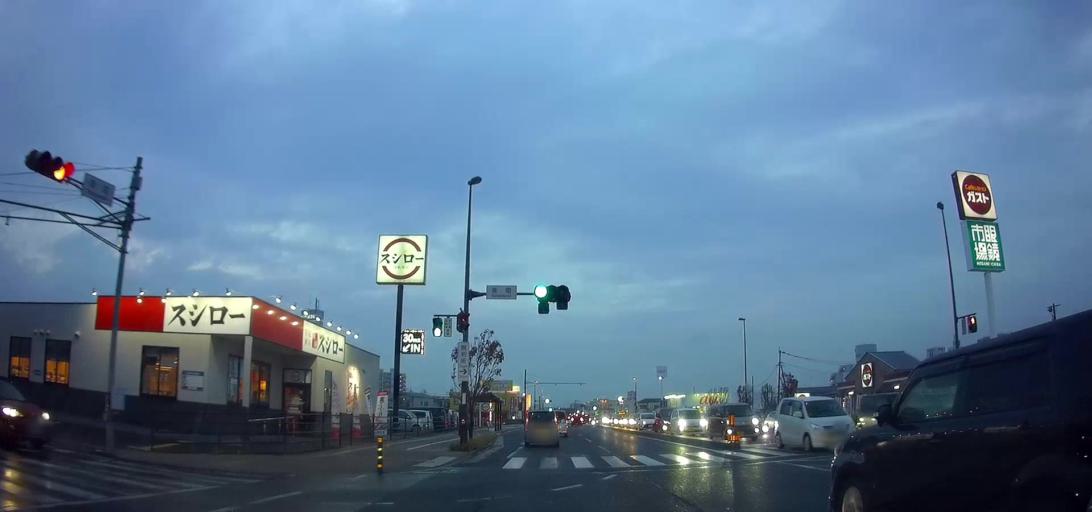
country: JP
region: Nagasaki
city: Omura
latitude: 32.9030
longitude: 129.9579
